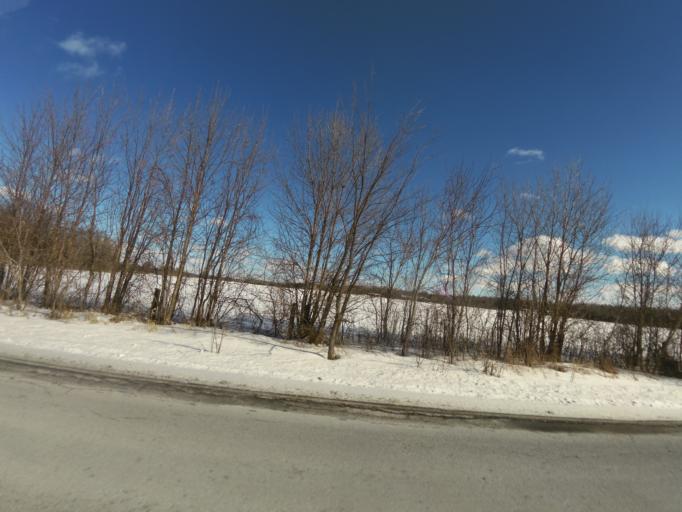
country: CA
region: Ontario
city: Ottawa
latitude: 45.2810
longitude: -75.5254
